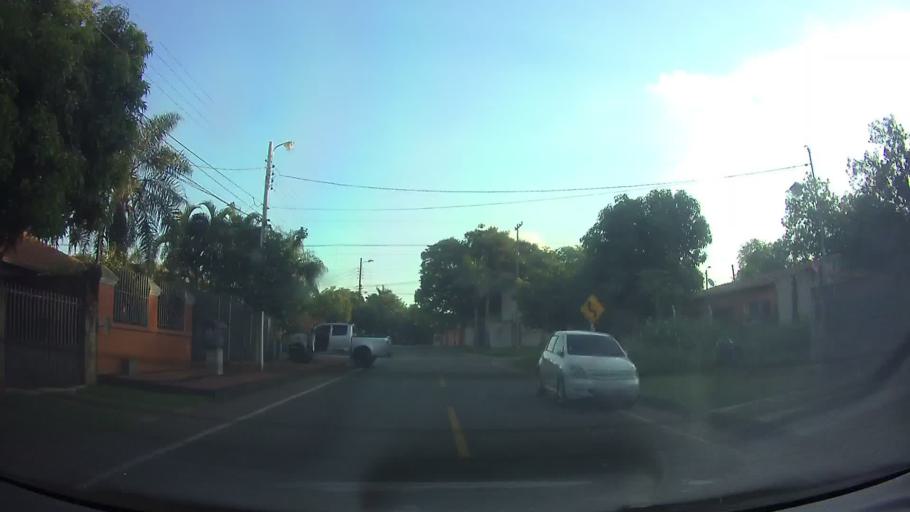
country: PY
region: Central
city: San Lorenzo
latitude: -25.2533
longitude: -57.4986
